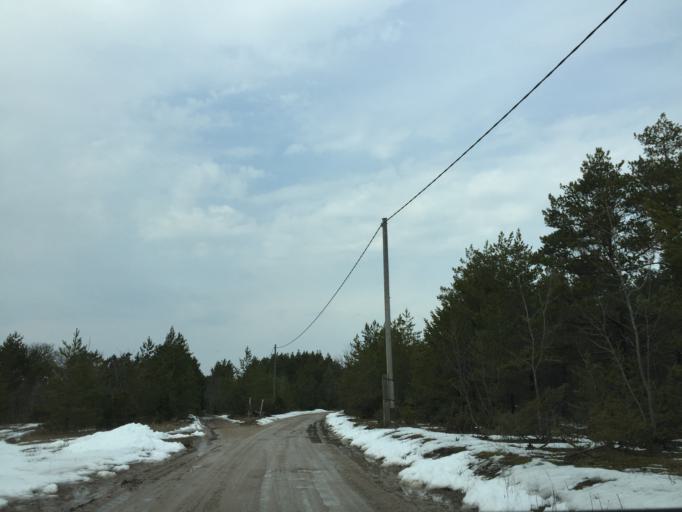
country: EE
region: Saare
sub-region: Kuressaare linn
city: Kuressaare
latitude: 58.4281
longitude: 22.1449
